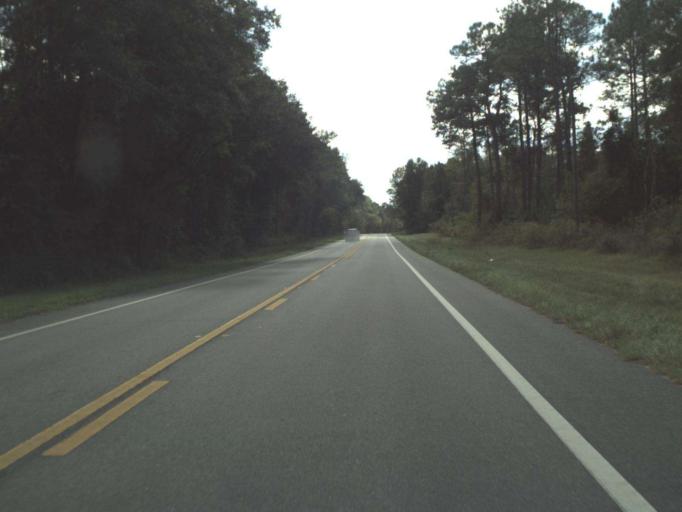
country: US
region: Florida
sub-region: Holmes County
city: Bonifay
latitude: 30.7191
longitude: -85.6160
